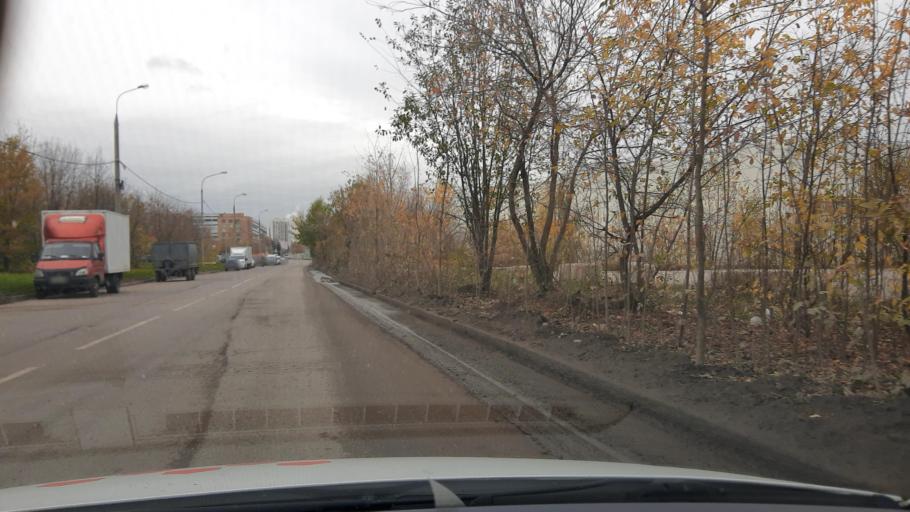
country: RU
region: Moscow
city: Tsaritsyno
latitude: 55.6188
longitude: 37.6301
